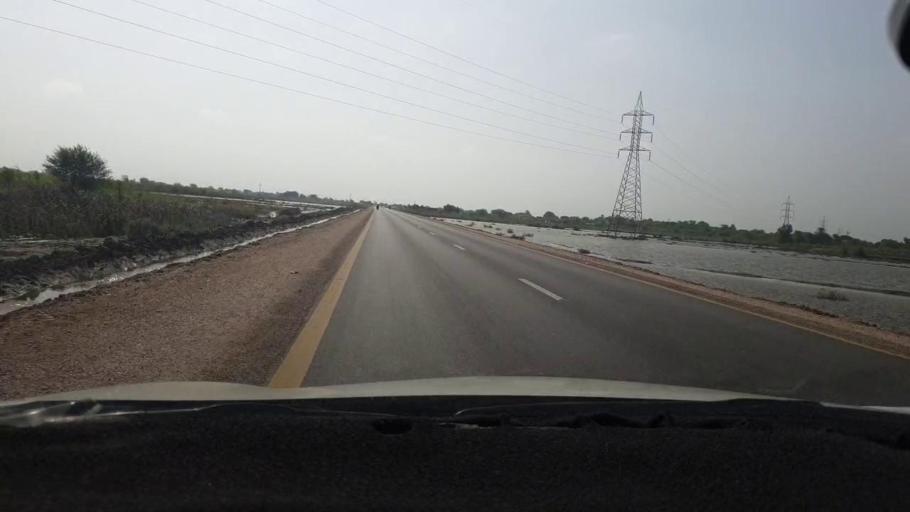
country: PK
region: Sindh
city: Jhol
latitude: 25.8634
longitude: 69.0545
